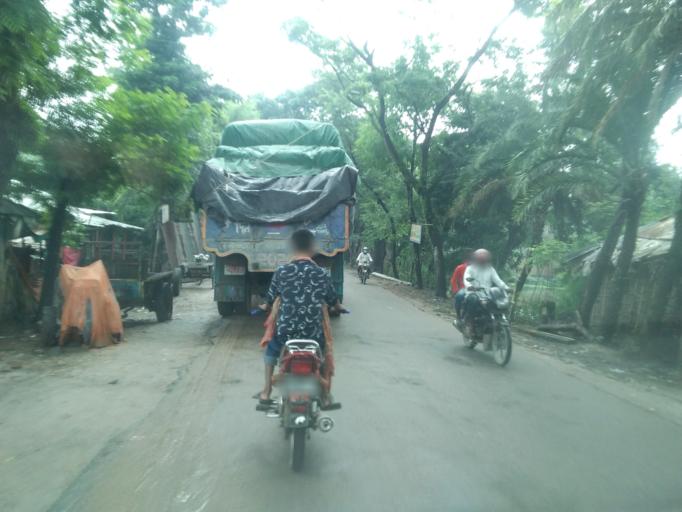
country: IN
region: West Bengal
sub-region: North 24 Parganas
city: Taki
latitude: 22.3476
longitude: 89.1038
